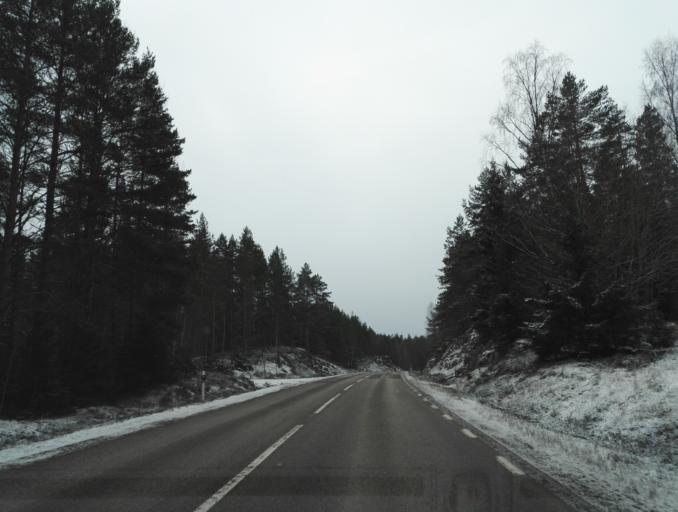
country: SE
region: Kalmar
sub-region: Hultsfreds Kommun
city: Virserum
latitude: 57.2727
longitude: 15.5701
